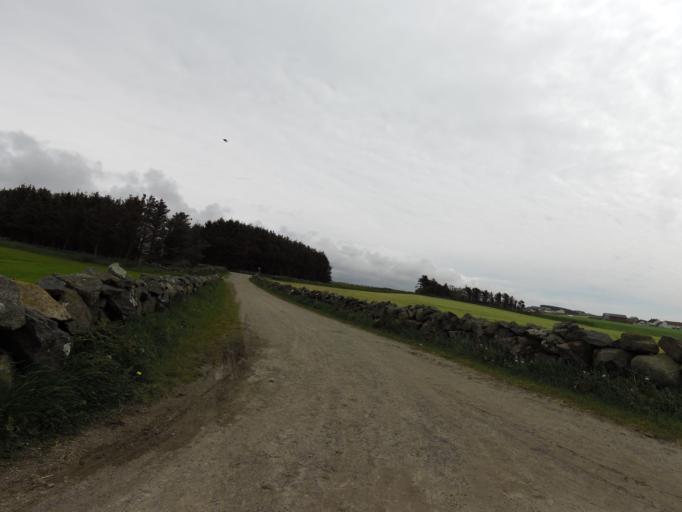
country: NO
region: Rogaland
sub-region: Ha
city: Naerbo
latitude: 58.6720
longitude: 5.5497
